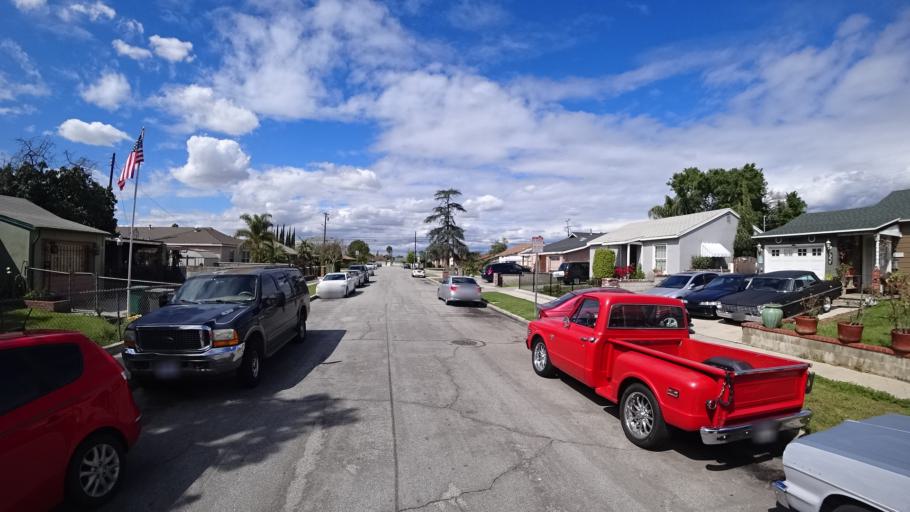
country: US
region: California
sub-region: Los Angeles County
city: Baldwin Park
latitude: 34.0979
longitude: -117.9686
